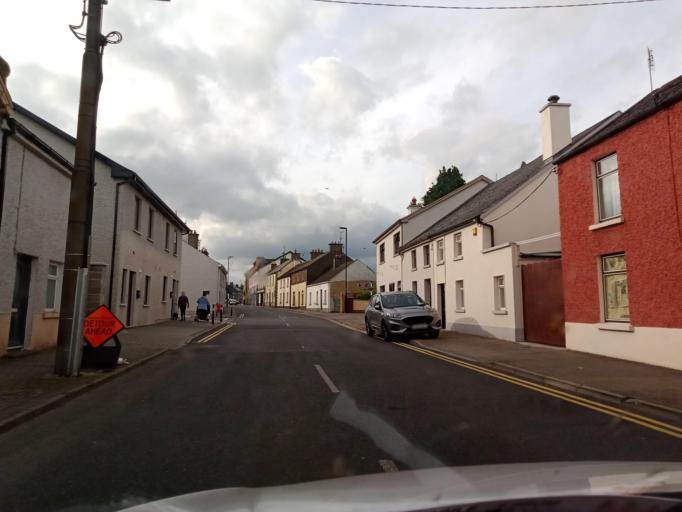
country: IE
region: Leinster
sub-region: Laois
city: Mountrath
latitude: 52.9999
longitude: -7.4721
